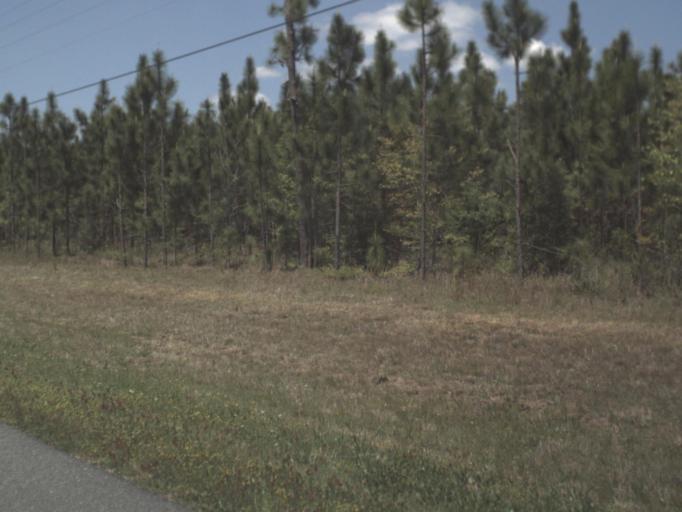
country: US
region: Alabama
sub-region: Escambia County
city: East Brewton
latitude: 30.9457
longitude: -87.0328
